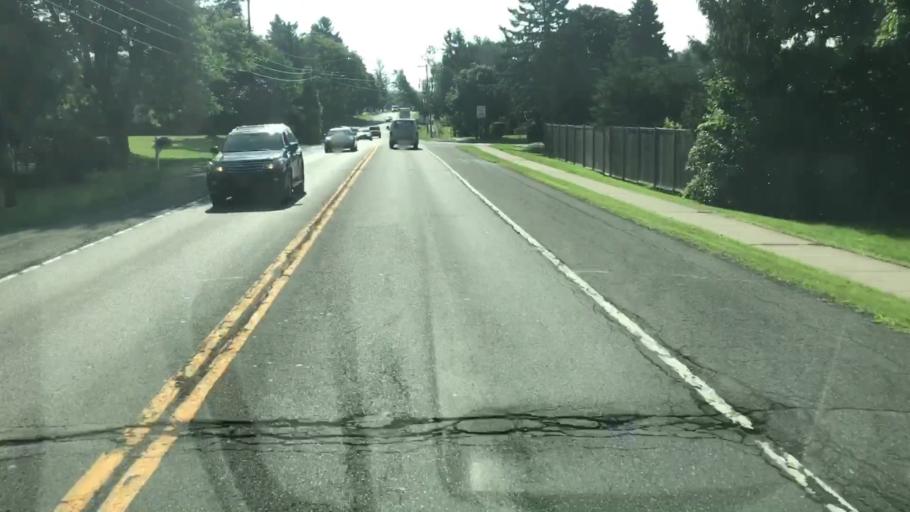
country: US
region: New York
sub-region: Onondaga County
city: Manlius
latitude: 43.0082
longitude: -75.9899
